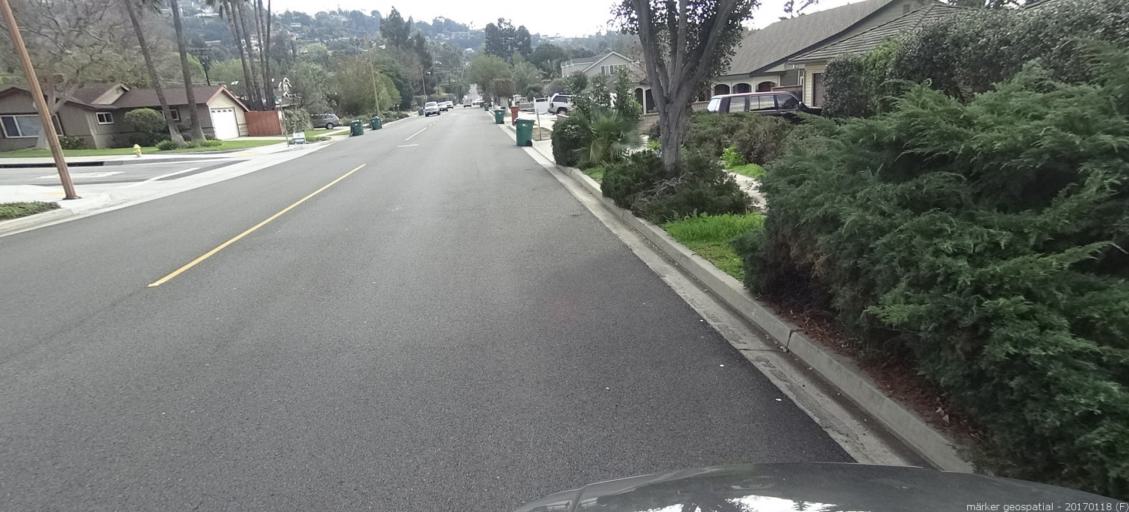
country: US
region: California
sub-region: Orange County
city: North Tustin
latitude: 33.7652
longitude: -117.7931
